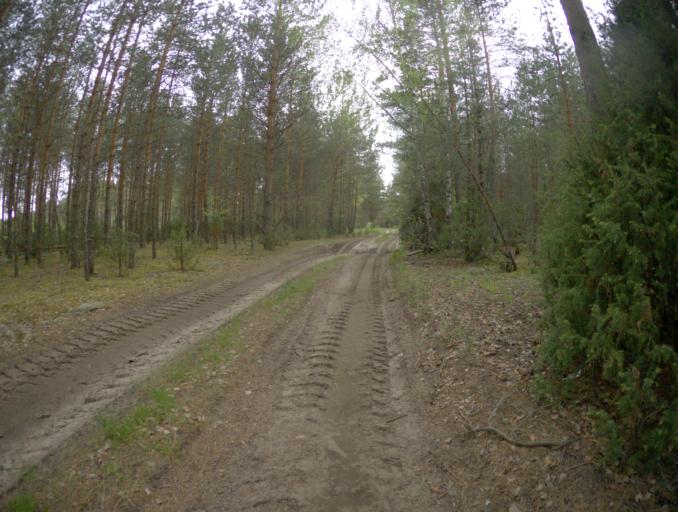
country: RU
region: Rjazan
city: Gus'-Zheleznyy
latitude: 55.1251
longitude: 41.1401
